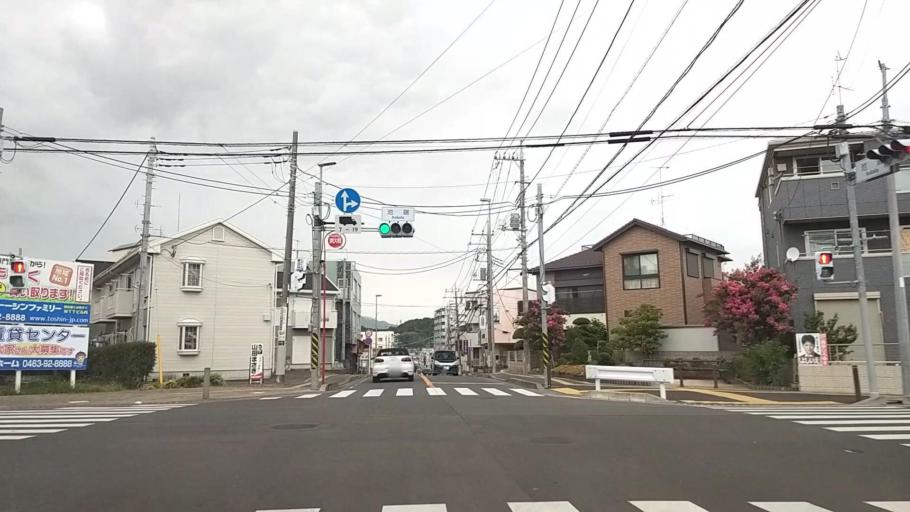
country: JP
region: Kanagawa
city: Isehara
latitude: 35.3989
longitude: 139.3152
